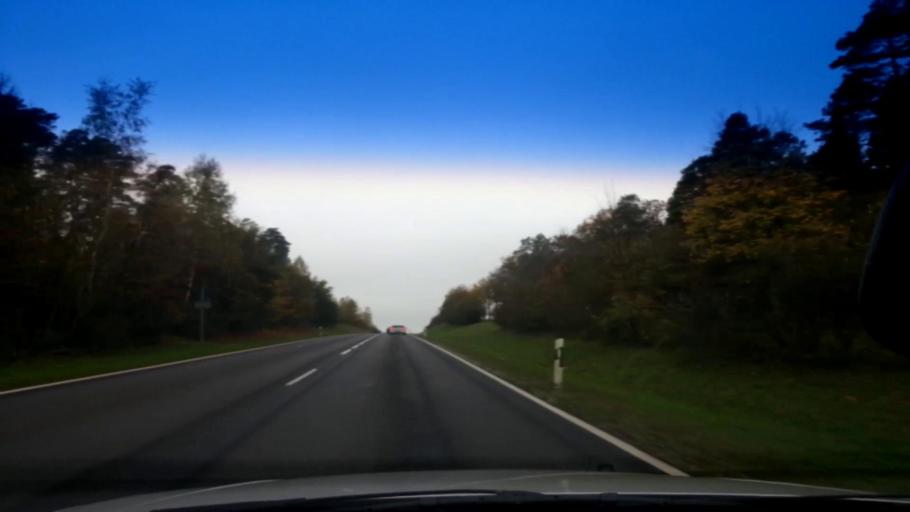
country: DE
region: Bavaria
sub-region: Upper Franconia
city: Stegaurach
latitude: 49.8349
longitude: 10.8134
